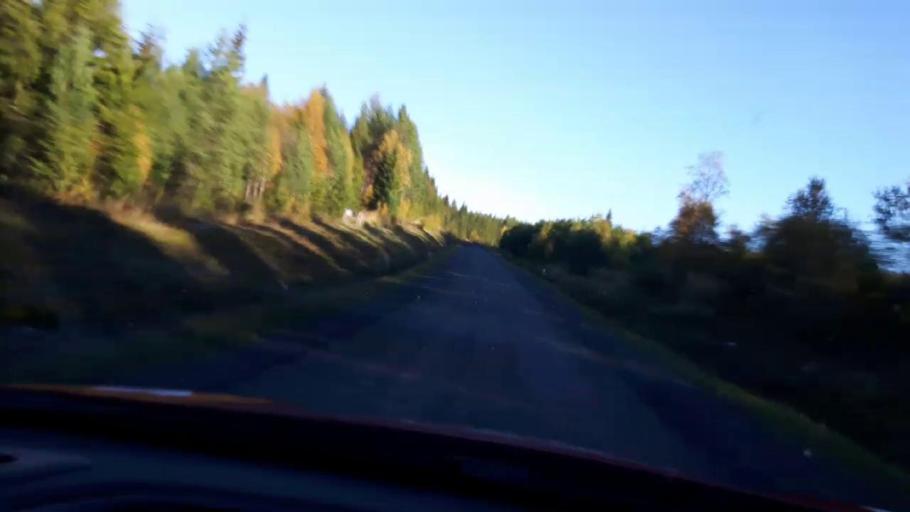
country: SE
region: Jaemtland
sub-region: OEstersunds Kommun
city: Lit
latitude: 63.5858
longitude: 14.8499
